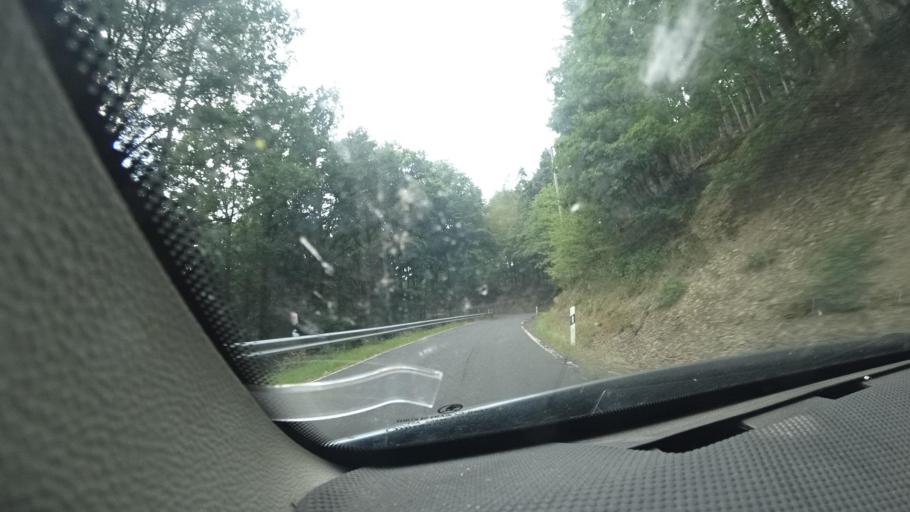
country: DE
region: Rheinland-Pfalz
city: Spessart
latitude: 50.4648
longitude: 7.0915
